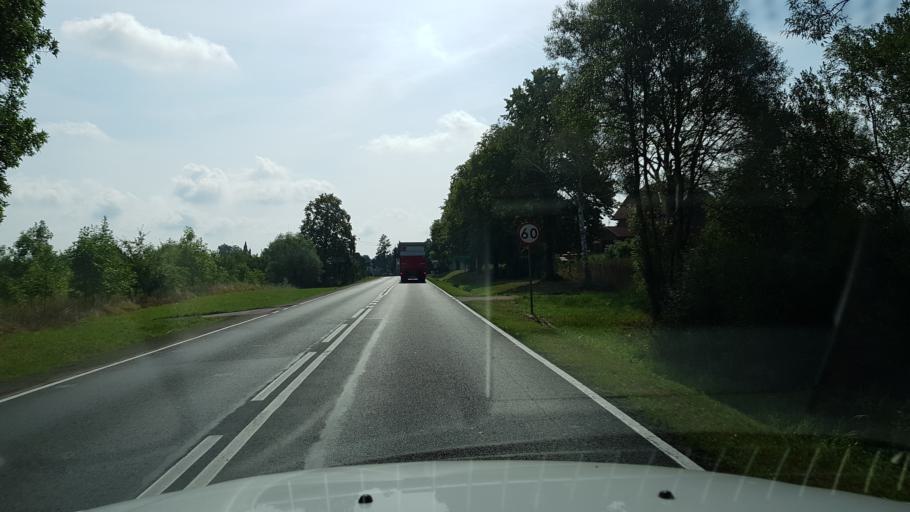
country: PL
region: West Pomeranian Voivodeship
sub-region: Powiat walecki
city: Walcz
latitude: 53.3323
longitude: 16.2896
